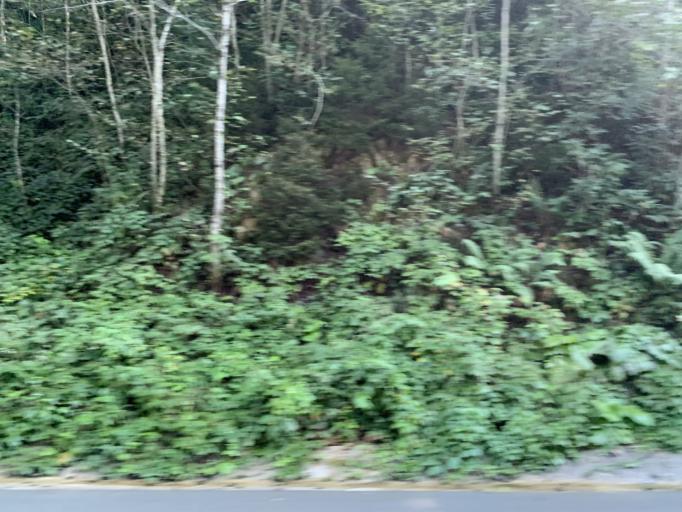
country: TR
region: Trabzon
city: Macka
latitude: 40.7065
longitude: 39.6500
